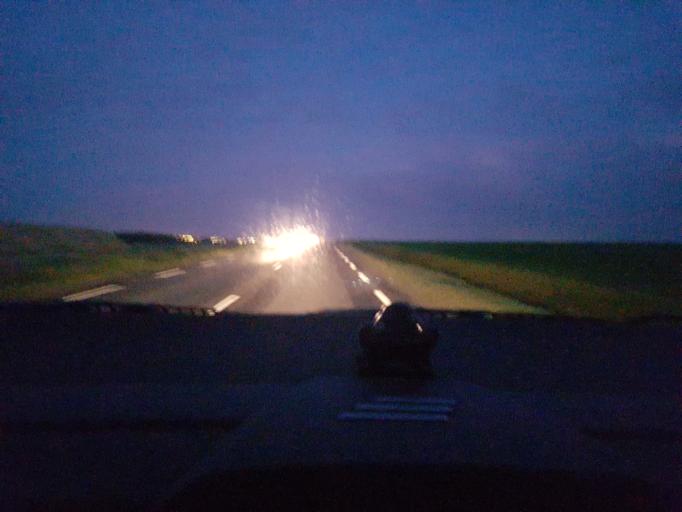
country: FR
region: Nord-Pas-de-Calais
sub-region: Departement du Pas-de-Calais
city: Riviere
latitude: 50.2619
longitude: 2.6978
